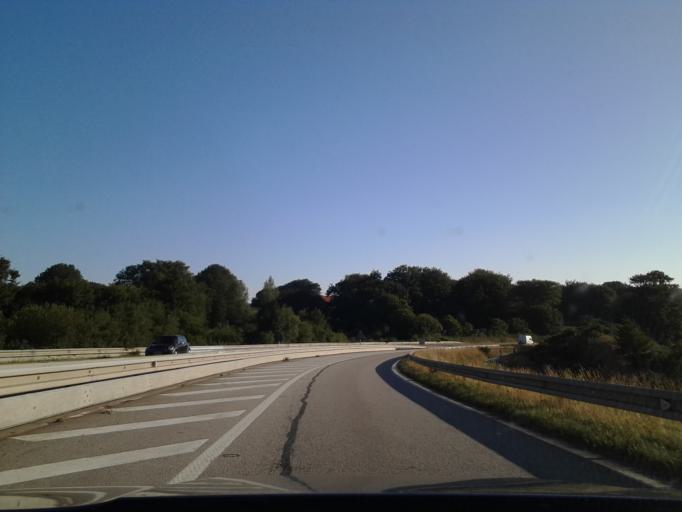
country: FR
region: Lower Normandy
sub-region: Departement de la Manche
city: La Glacerie
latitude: 49.6041
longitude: -1.5944
